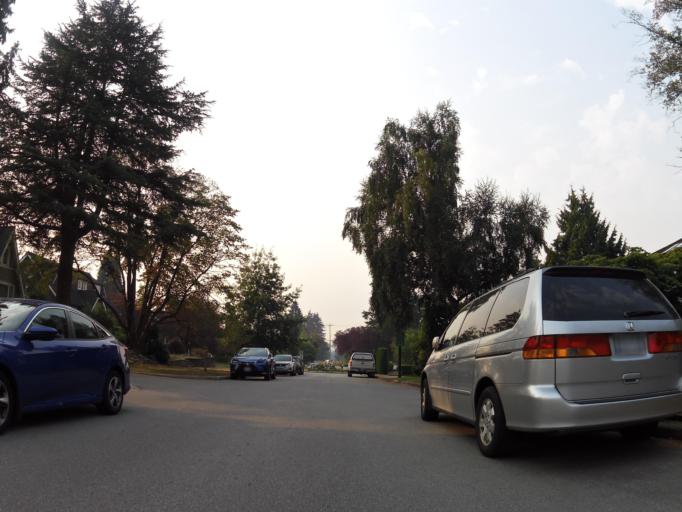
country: CA
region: British Columbia
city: Vancouver
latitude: 49.2185
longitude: -123.1484
